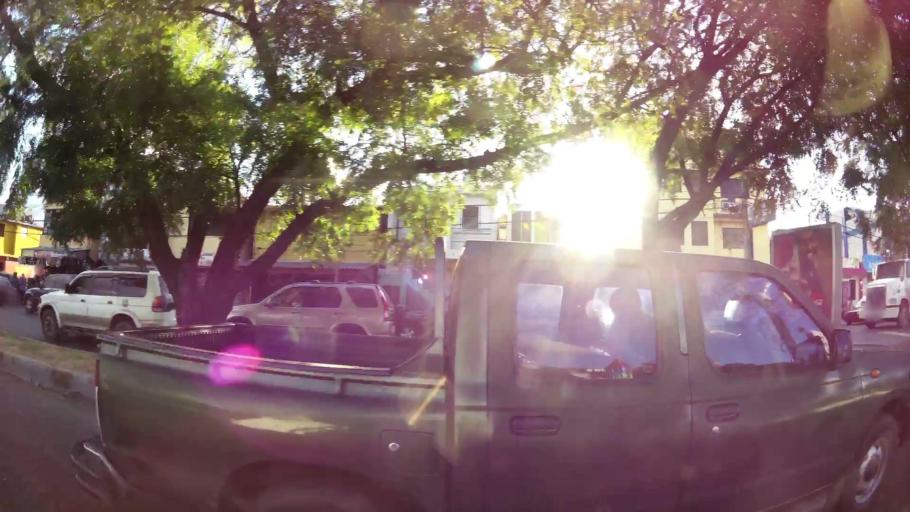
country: DO
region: Santiago
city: Santiago de los Caballeros
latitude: 19.4755
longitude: -70.7158
